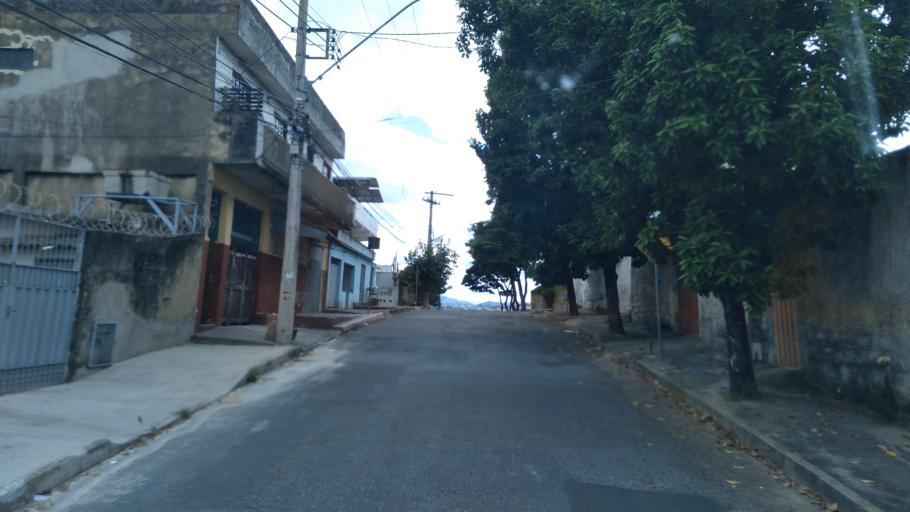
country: BR
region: Minas Gerais
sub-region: Belo Horizonte
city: Belo Horizonte
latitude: -19.8617
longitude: -43.9149
